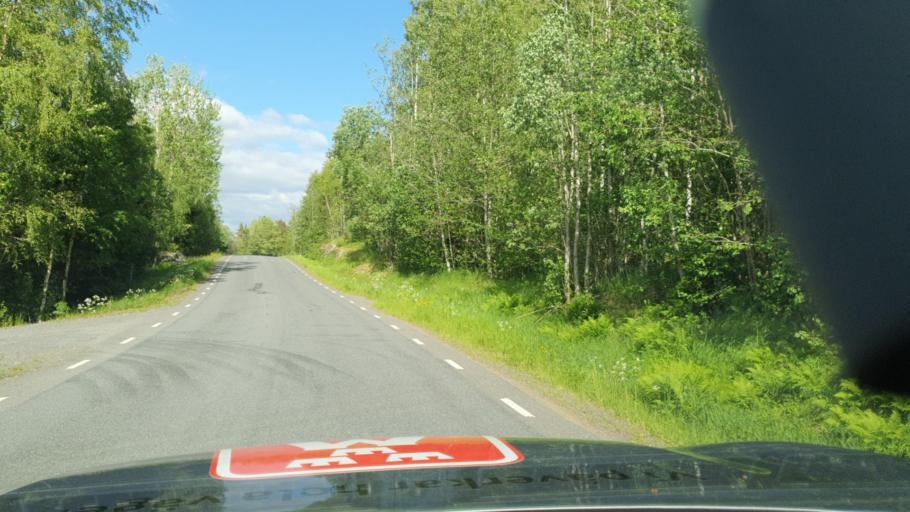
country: SE
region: Vaesternorrland
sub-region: Kramfors Kommun
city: Nordingra
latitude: 62.8101
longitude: 18.1340
